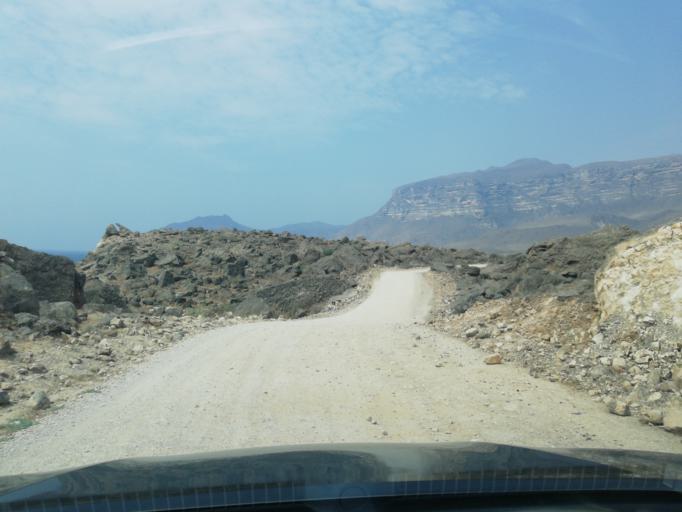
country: OM
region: Zufar
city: Salalah
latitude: 16.8173
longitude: 53.6934
